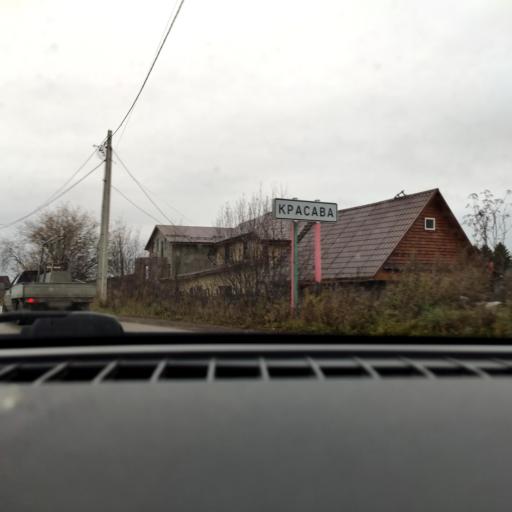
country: RU
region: Perm
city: Ferma
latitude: 57.9196
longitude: 56.3267
